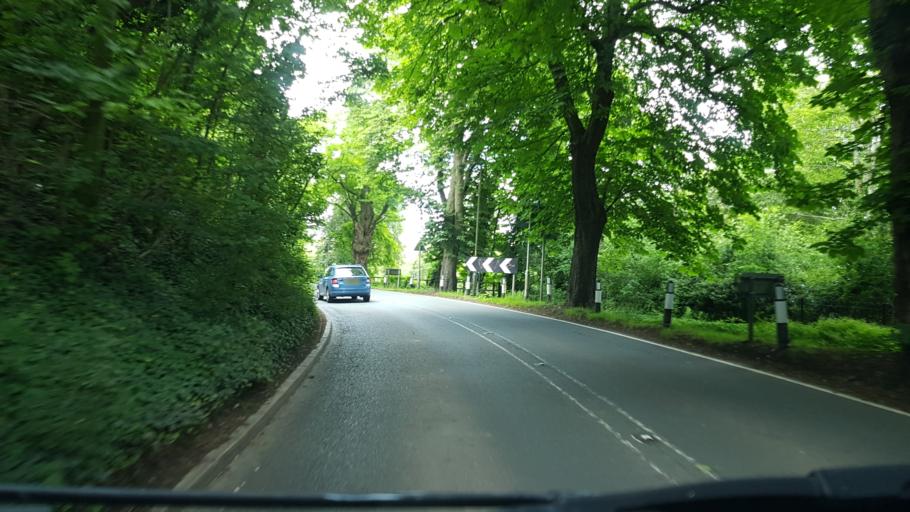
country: GB
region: England
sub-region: Worcestershire
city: Droitwich
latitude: 52.2673
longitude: -2.1353
